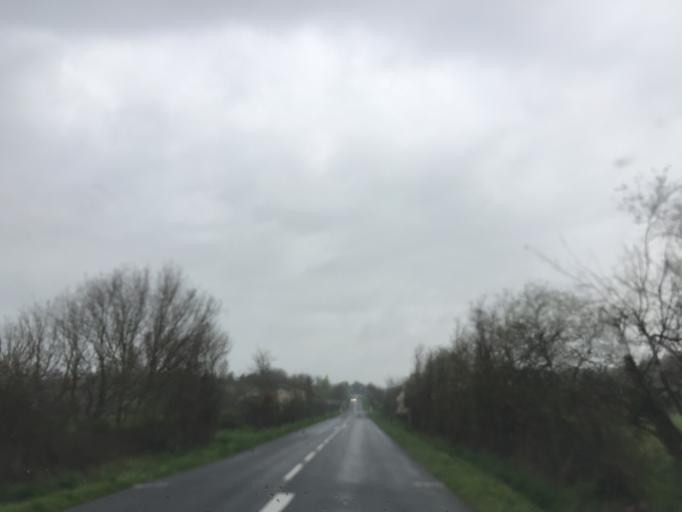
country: FR
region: Pays de la Loire
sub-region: Departement de la Loire-Atlantique
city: Casson
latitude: 47.3899
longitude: -1.5252
